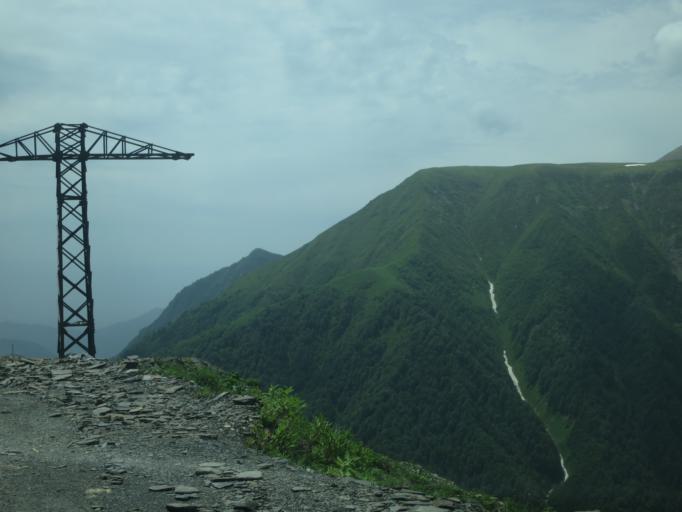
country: GE
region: Kakheti
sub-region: Telavi
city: Telavi
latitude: 42.2622
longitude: 45.5028
